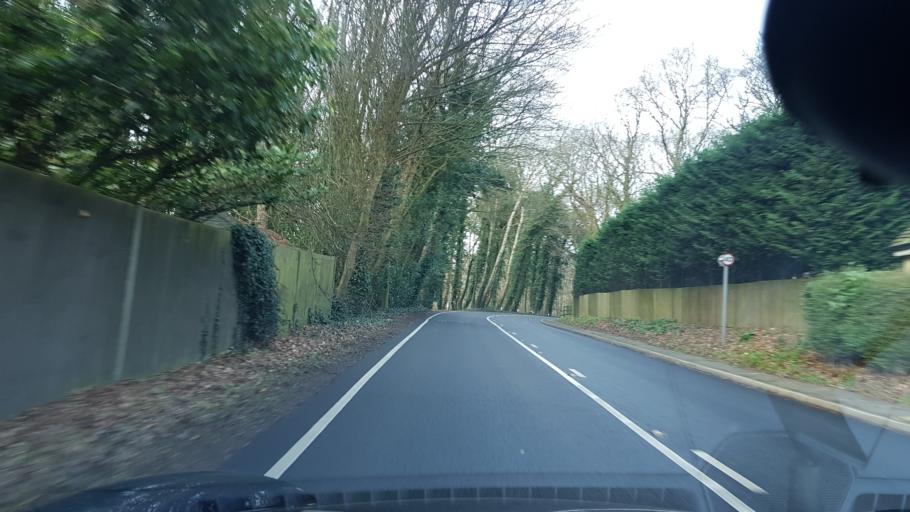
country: GB
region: England
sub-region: Surrey
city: Milford
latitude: 51.2165
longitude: -0.6494
